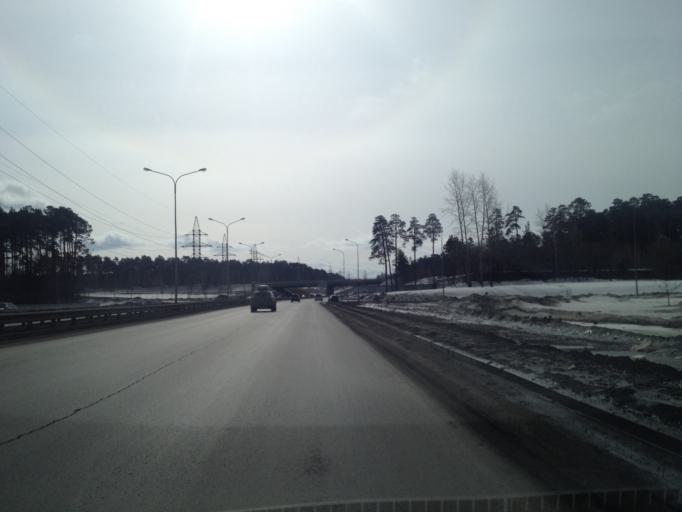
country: RU
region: Sverdlovsk
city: Sovkhoznyy
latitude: 56.7936
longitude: 60.5968
